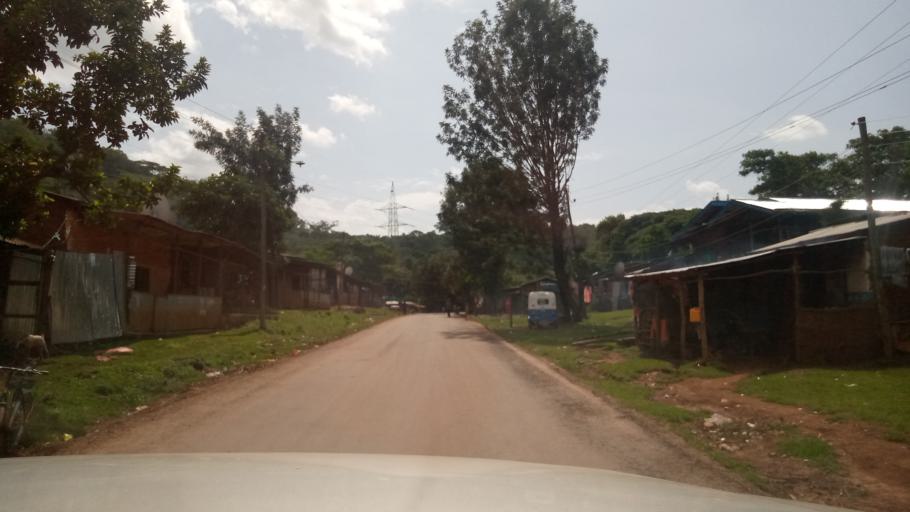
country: ET
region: Oromiya
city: Agaro
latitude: 7.9214
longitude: 36.5186
